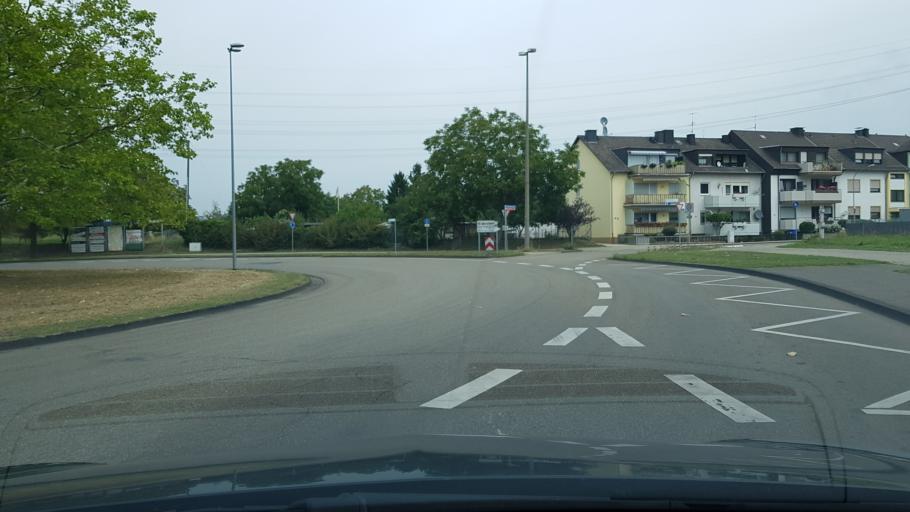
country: DE
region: Rheinland-Pfalz
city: Niederwerth
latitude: 50.3825
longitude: 7.6041
